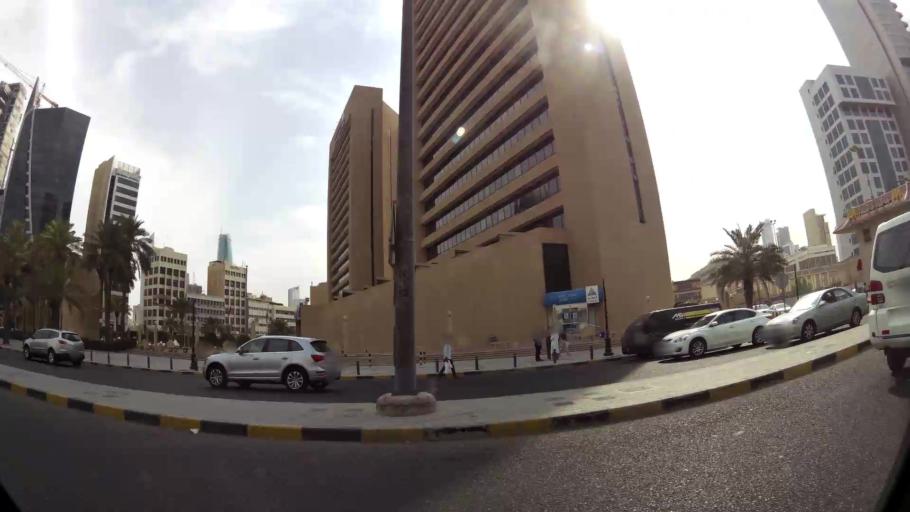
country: KW
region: Al Asimah
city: Kuwait City
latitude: 29.3748
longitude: 47.9765
